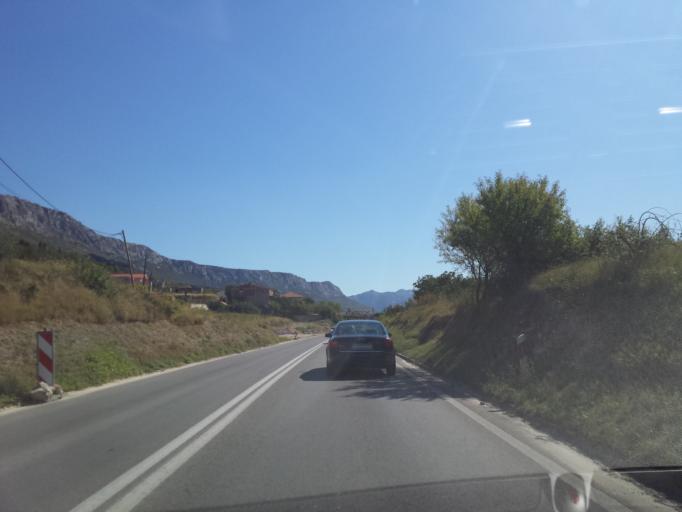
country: HR
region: Splitsko-Dalmatinska
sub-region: Grad Split
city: Split
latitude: 43.5574
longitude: 16.3840
